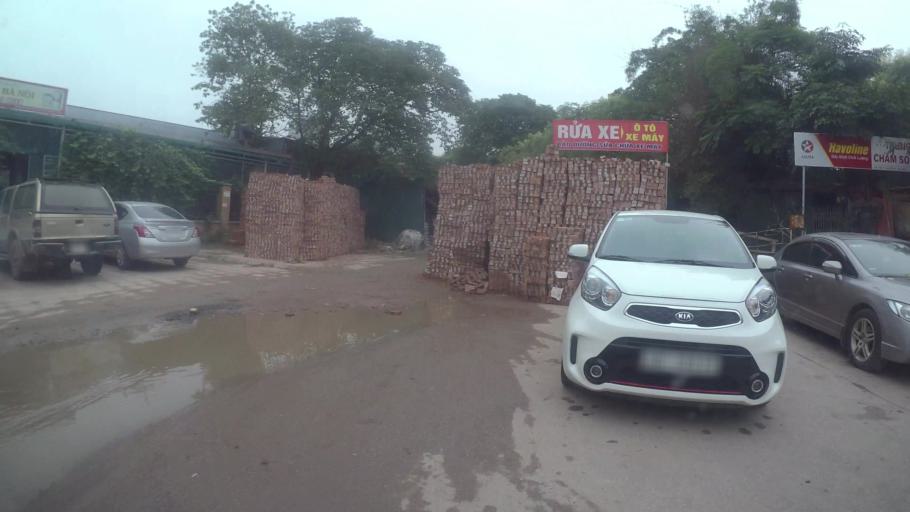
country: VN
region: Ha Noi
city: Dong Da
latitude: 21.0333
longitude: 105.8198
